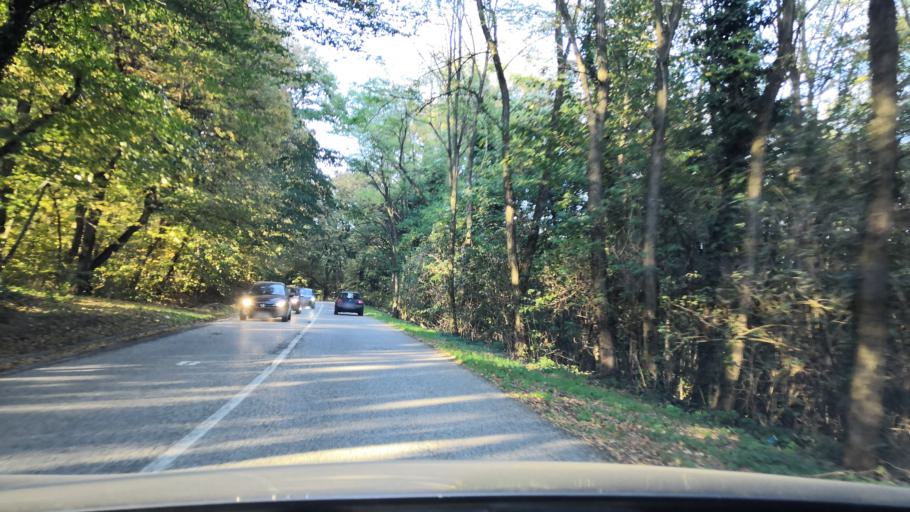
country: RS
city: Vrdnik
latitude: 45.1487
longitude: 19.7771
